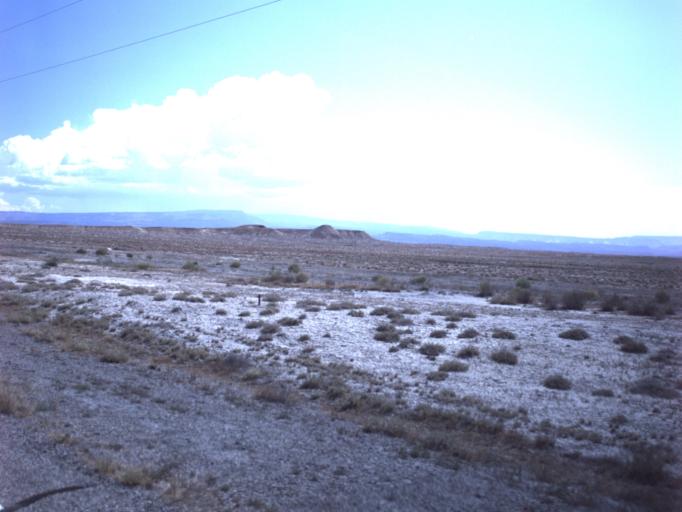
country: US
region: Utah
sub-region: Grand County
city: Moab
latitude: 38.9388
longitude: -109.3888
